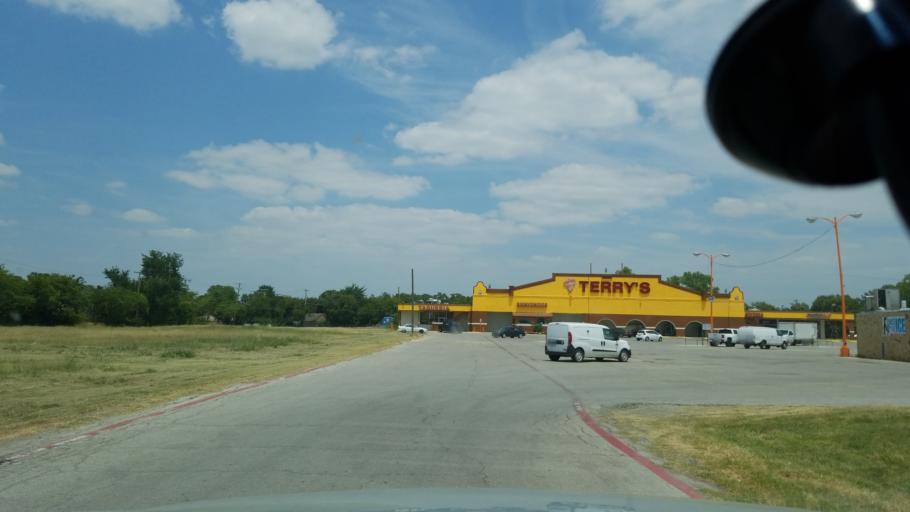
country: US
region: Texas
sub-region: Dallas County
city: Grand Prairie
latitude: 32.7493
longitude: -96.9790
